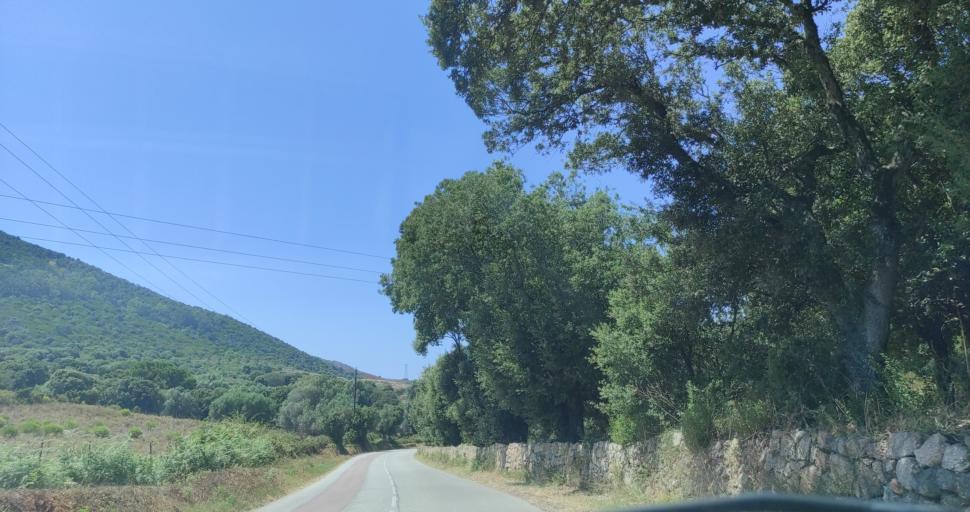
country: FR
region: Corsica
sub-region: Departement de la Corse-du-Sud
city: Alata
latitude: 41.9634
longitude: 8.7234
